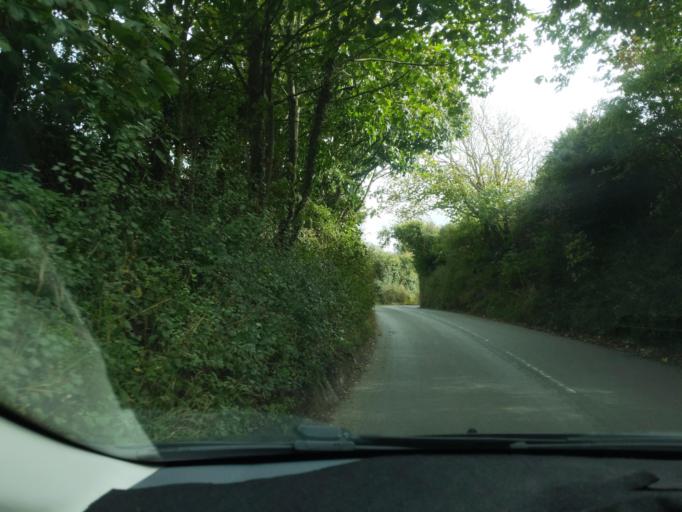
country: GB
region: England
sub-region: Cornwall
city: Mevagissey
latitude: 50.2457
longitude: -4.8069
